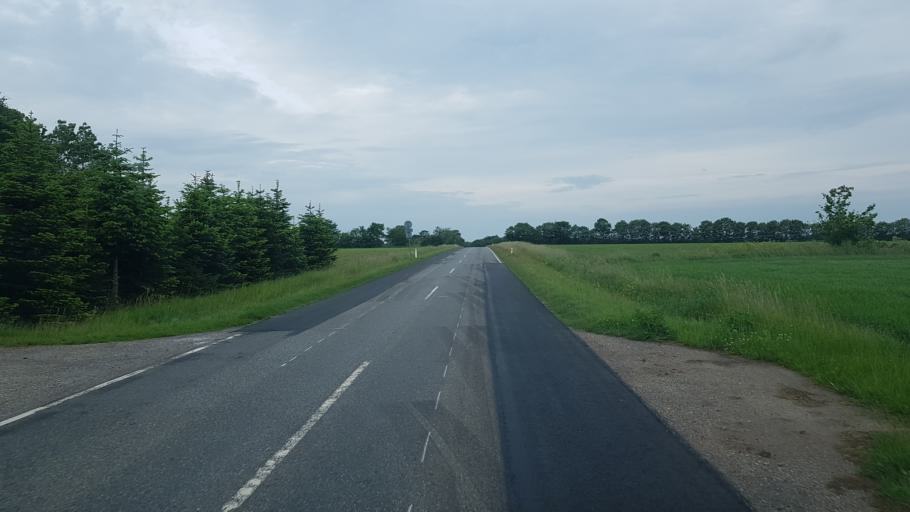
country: DK
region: South Denmark
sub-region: Vejen Kommune
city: Holsted
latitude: 55.4410
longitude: 8.9350
